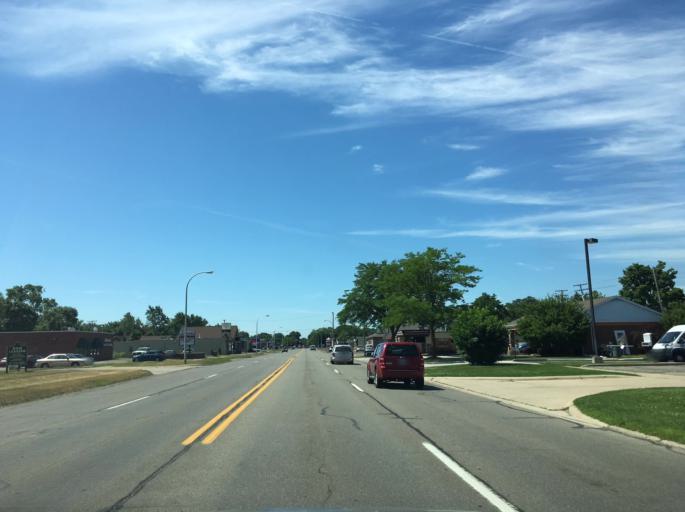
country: US
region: Michigan
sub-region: Wayne County
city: Allen Park
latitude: 42.2542
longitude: -83.2155
